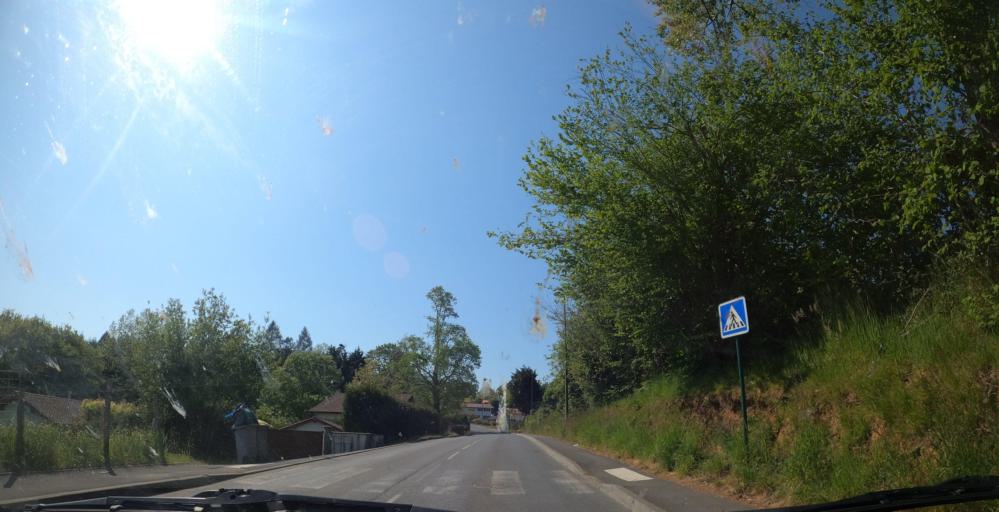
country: FR
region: Aquitaine
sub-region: Departement des Pyrenees-Atlantiques
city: Bassussarry
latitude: 43.4456
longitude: -1.5052
